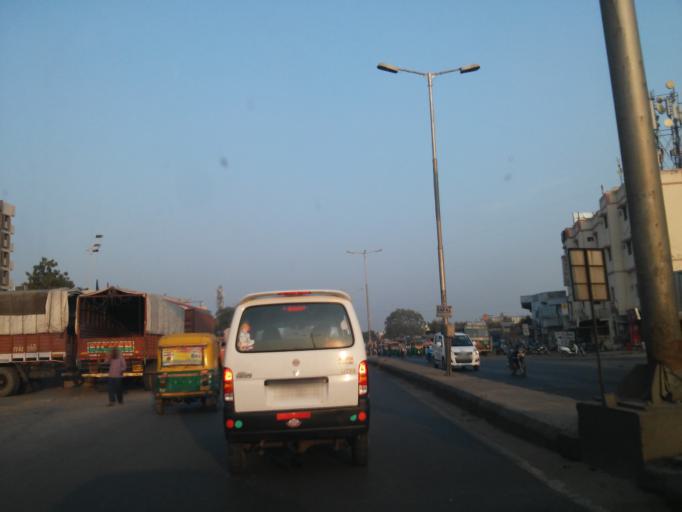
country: IN
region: Gujarat
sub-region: Ahmadabad
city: Sarkhej
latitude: 22.9881
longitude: 72.5064
